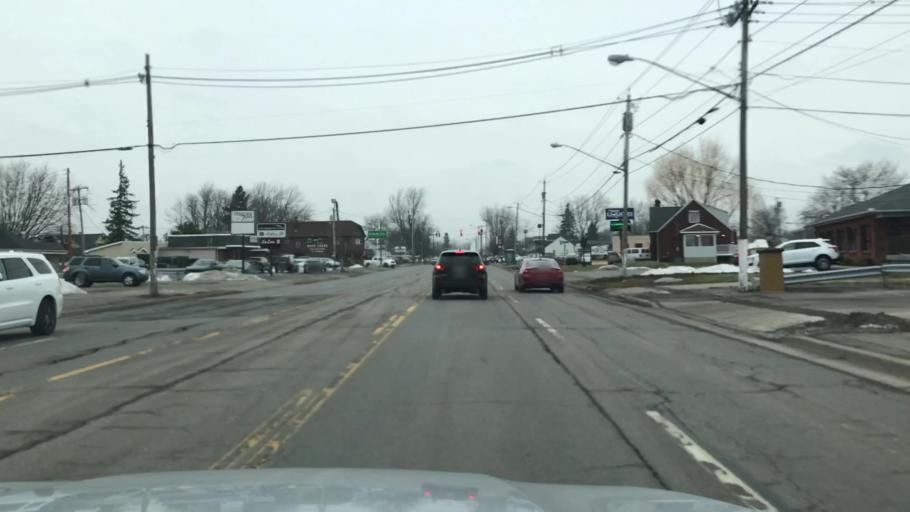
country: US
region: New York
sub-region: Erie County
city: Lackawanna
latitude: 42.8153
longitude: -78.8006
